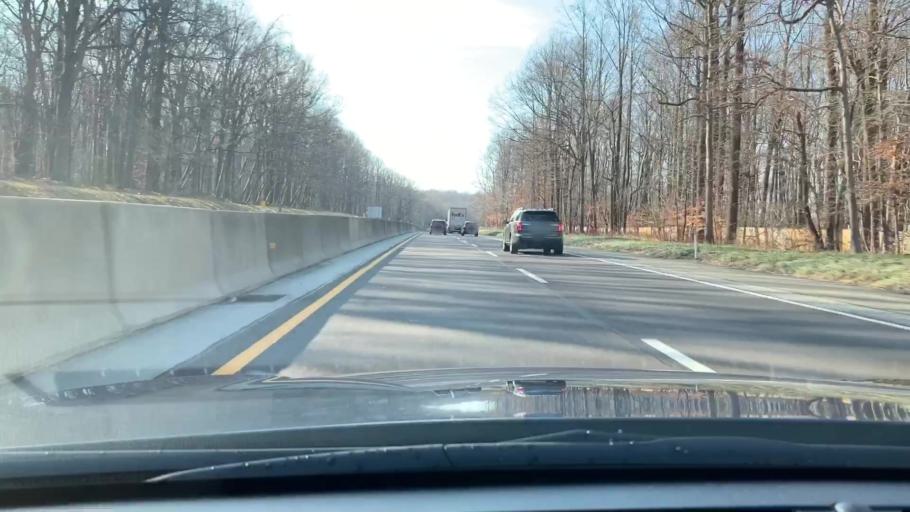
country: US
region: Pennsylvania
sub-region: Chester County
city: Chester Springs
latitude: 40.0682
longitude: -75.5751
